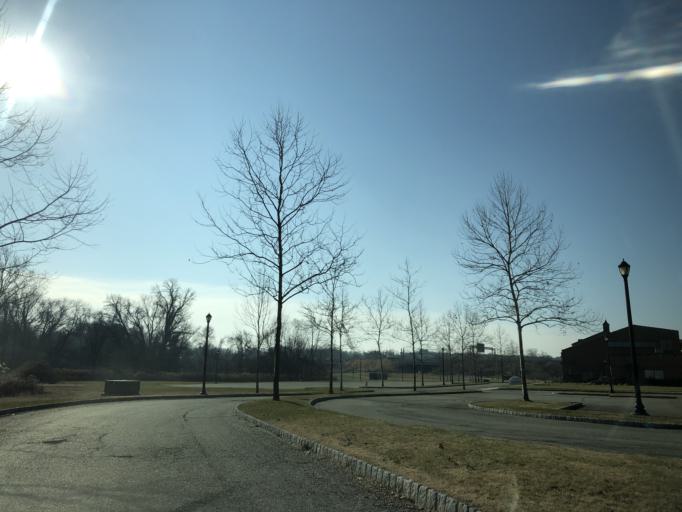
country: US
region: Pennsylvania
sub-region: Montgomery County
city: Audubon
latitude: 40.1112
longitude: -75.4163
